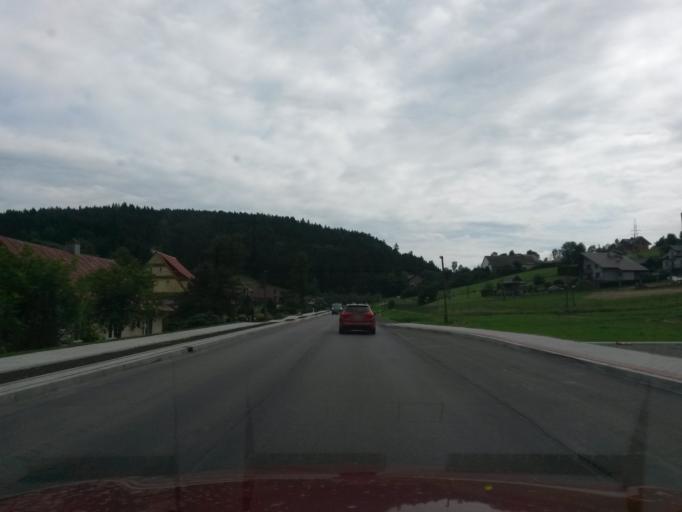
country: PL
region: Lesser Poland Voivodeship
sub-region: Powiat nowosadecki
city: Labowa
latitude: 49.4898
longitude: 20.9111
